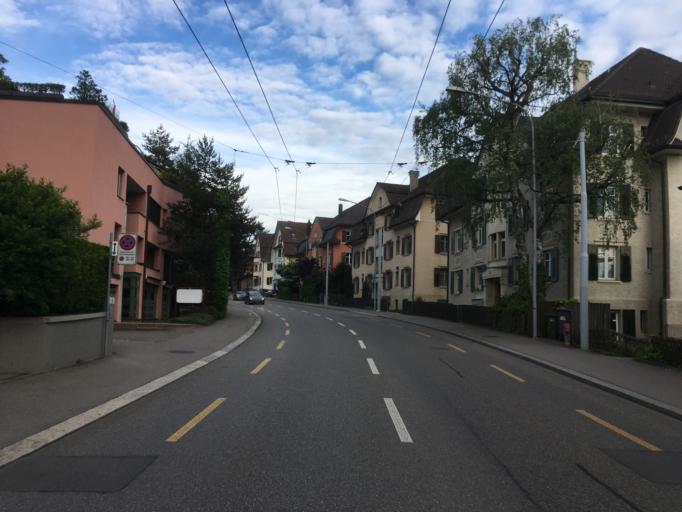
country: CH
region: Zurich
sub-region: Bezirk Zuerich
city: Zuerich (Kreis 7) / Hirslanden
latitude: 47.3620
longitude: 8.5692
